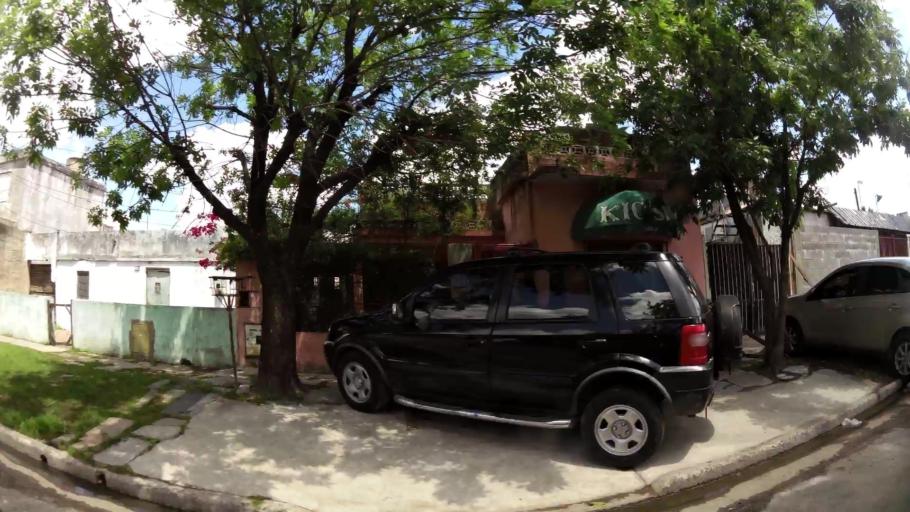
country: AR
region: Buenos Aires
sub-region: Partido de Lanus
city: Lanus
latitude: -34.6959
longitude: -58.4348
